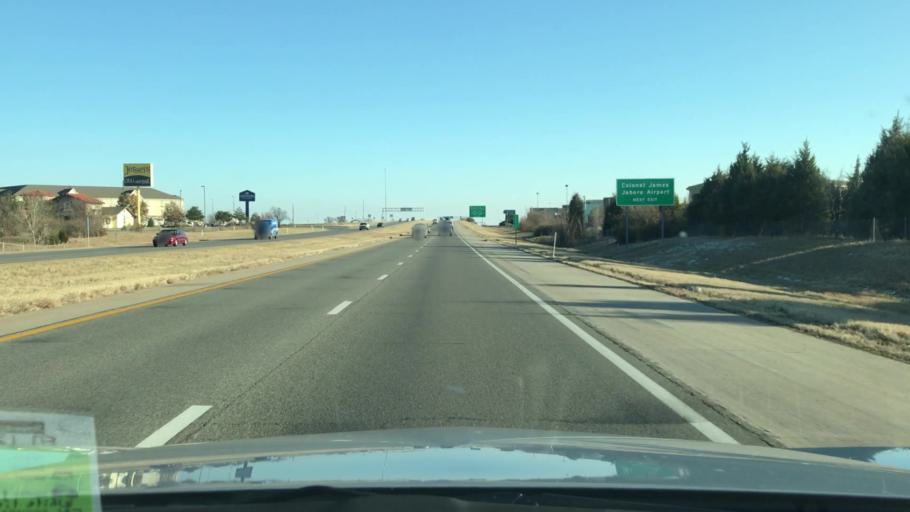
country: US
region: Kansas
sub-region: Sedgwick County
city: Bellaire
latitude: 37.7419
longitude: -97.2318
